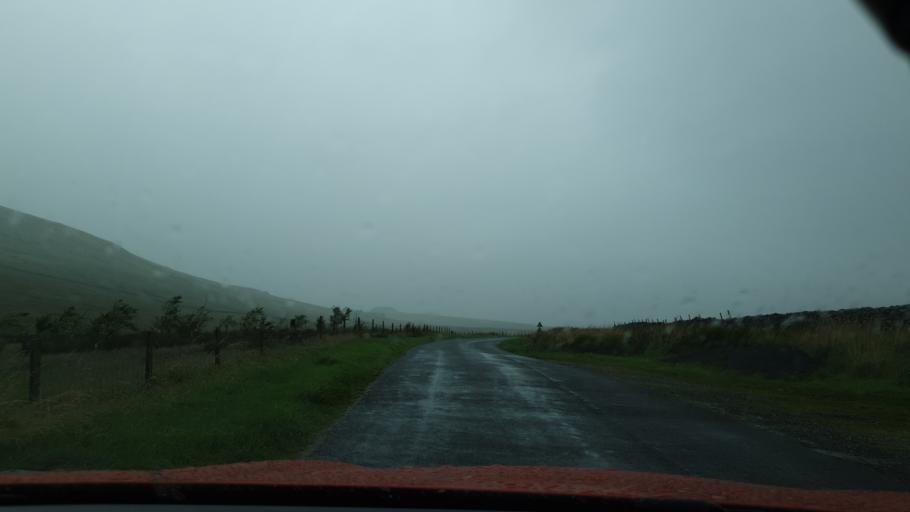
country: GB
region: England
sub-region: Cumbria
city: Millom
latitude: 54.3464
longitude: -3.2495
